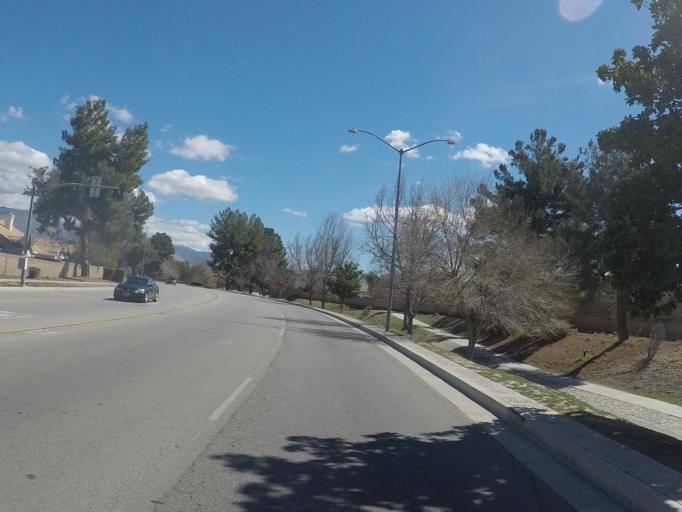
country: US
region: California
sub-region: Riverside County
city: San Jacinto
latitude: 33.7696
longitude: -116.9381
